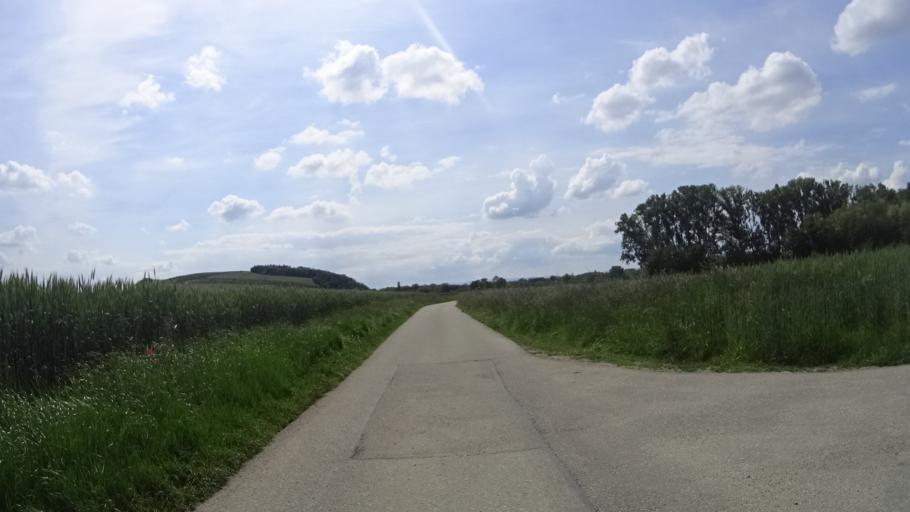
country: DE
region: Baden-Wuerttemberg
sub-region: Freiburg Region
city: Sasbach
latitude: 48.1591
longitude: 7.6237
